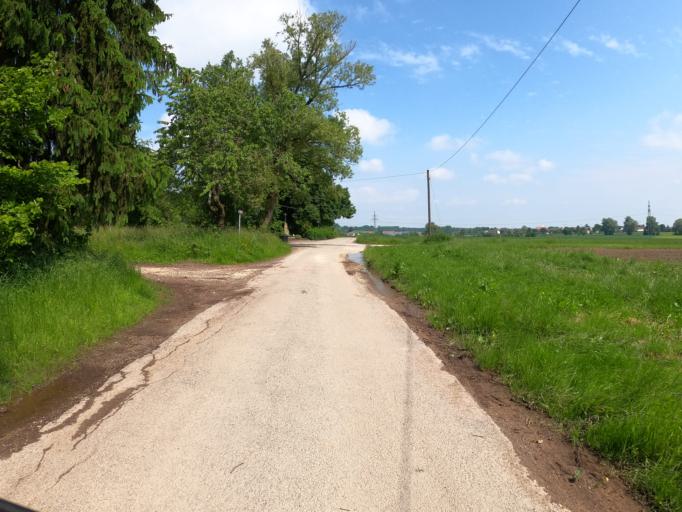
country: DE
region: Bavaria
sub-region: Swabia
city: Holzheim
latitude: 48.3696
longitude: 10.1000
